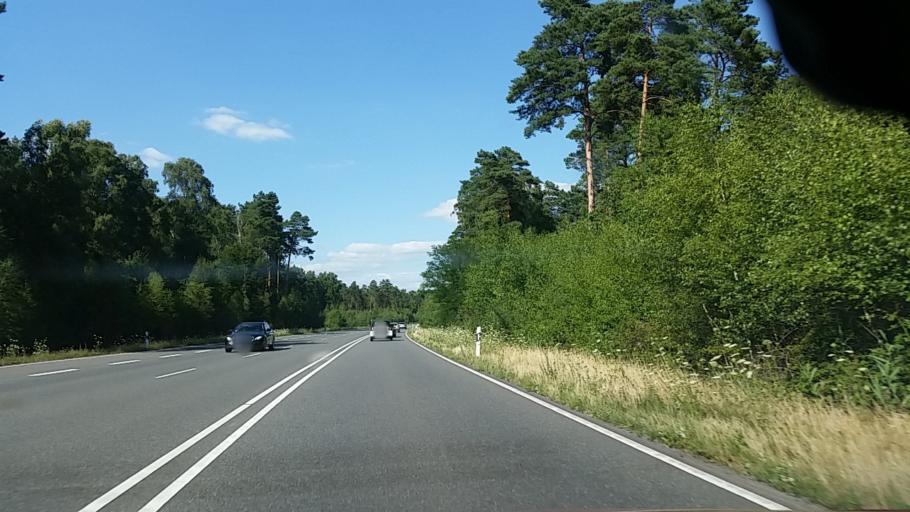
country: DE
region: Lower Saxony
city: Adelheidsdorf
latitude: 52.5565
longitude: 10.0691
